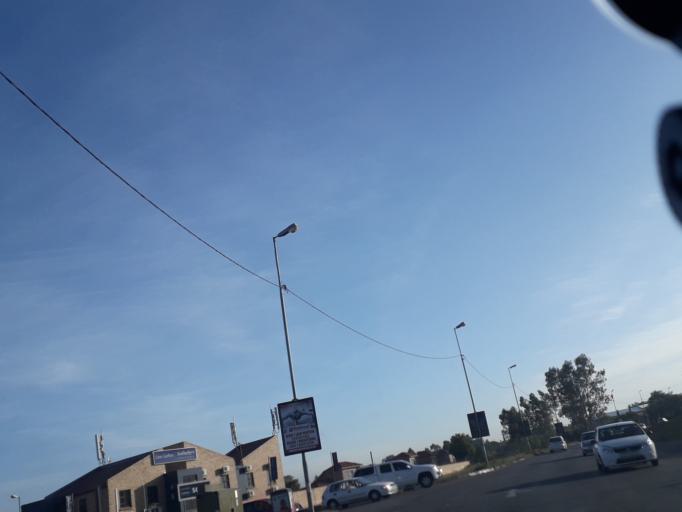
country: ZA
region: Gauteng
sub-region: City of Johannesburg Metropolitan Municipality
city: Roodepoort
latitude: -26.1027
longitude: 27.9002
